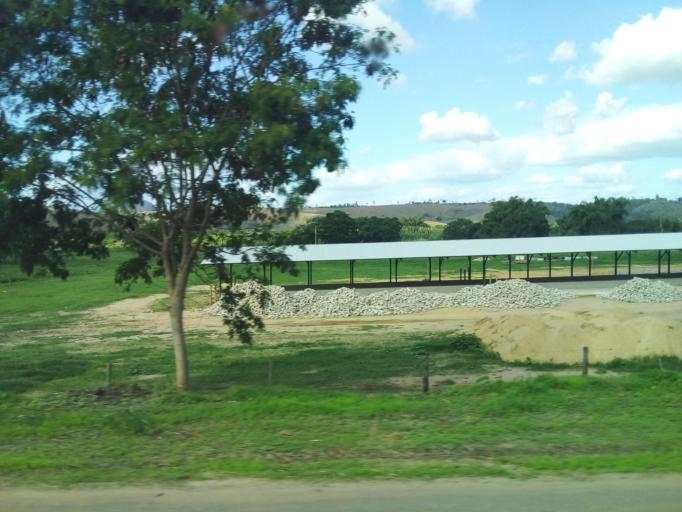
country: BR
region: Minas Gerais
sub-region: Conselheiro Pena
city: Conselheiro Pena
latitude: -18.9931
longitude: -41.5969
